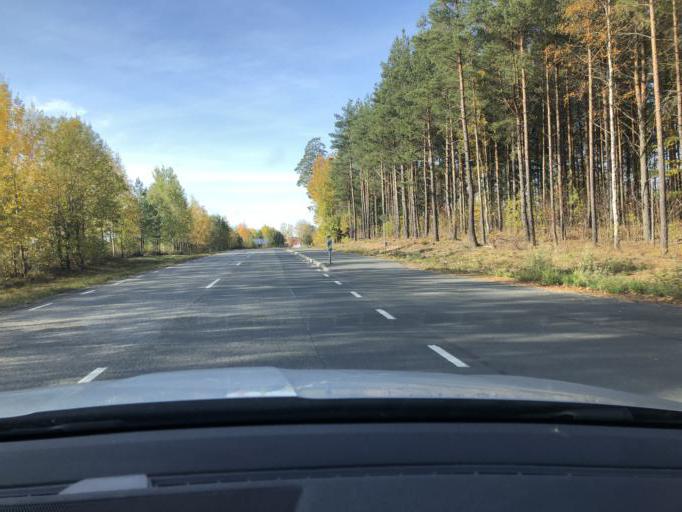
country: SE
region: Joenkoeping
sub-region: Jonkopings Kommun
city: Jonkoping
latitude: 57.7714
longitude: 14.0980
